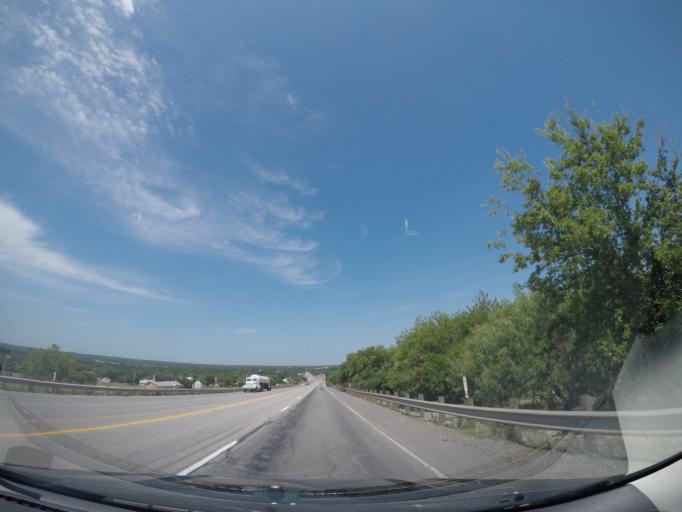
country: US
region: Texas
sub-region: Medina County
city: Castroville
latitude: 29.3497
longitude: -98.8912
